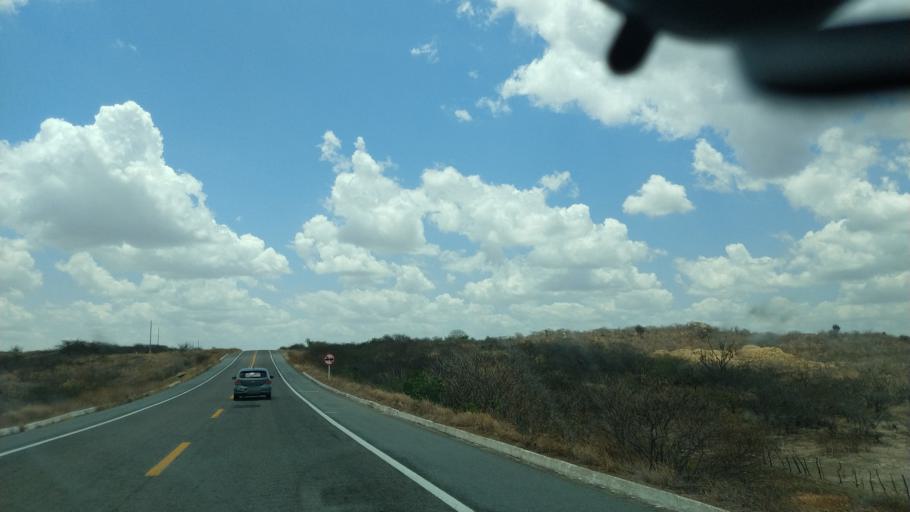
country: BR
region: Rio Grande do Norte
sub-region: Cerro Cora
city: Cerro Cora
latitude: -6.2035
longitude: -36.3284
